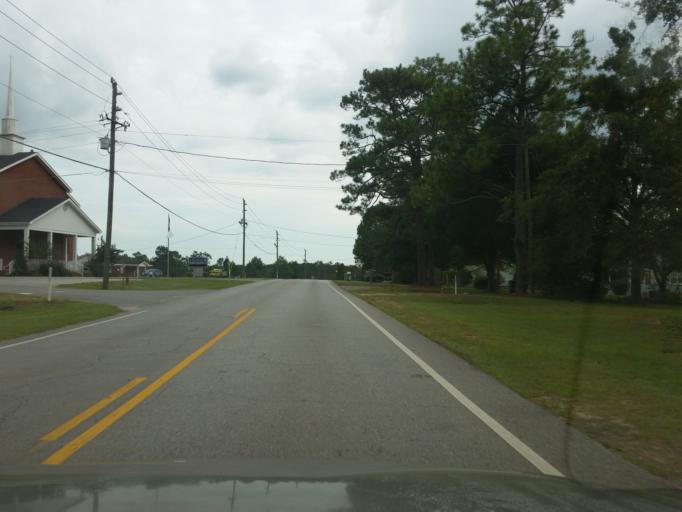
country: US
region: Florida
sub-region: Escambia County
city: Molino
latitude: 30.7132
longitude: -87.3367
